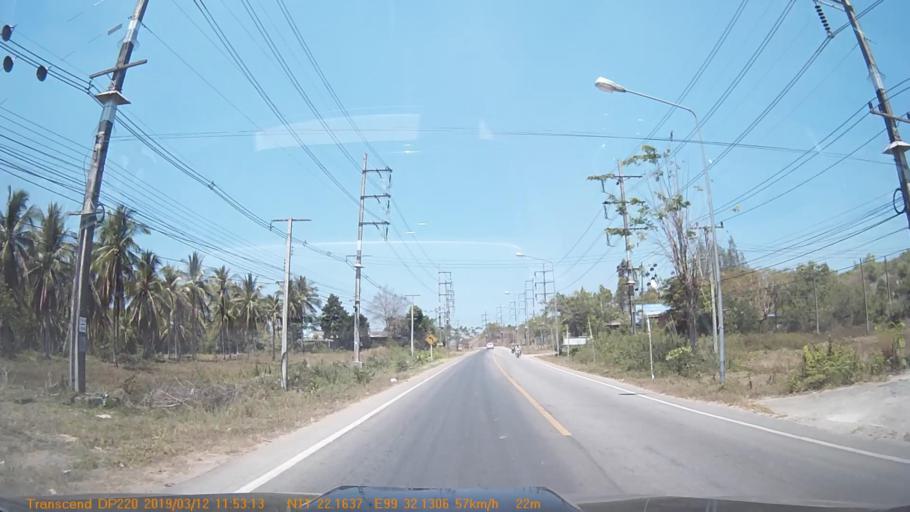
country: TH
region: Prachuap Khiri Khan
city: Thap Sakae
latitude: 11.3694
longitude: 99.5354
